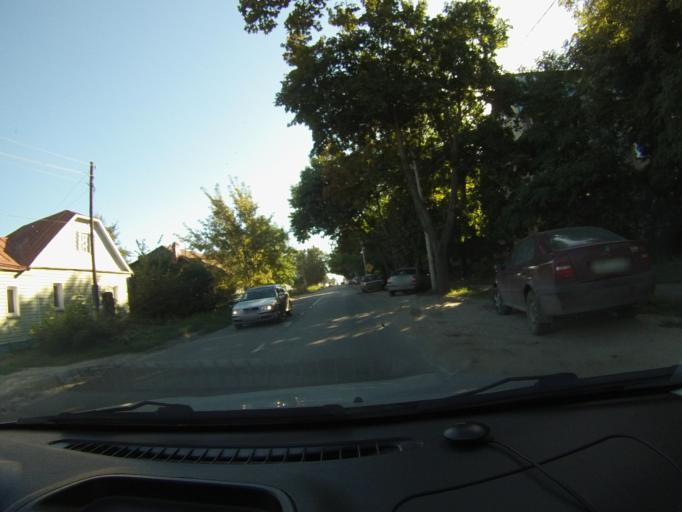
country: RU
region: Tambov
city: Tambov
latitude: 52.7495
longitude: 41.4223
